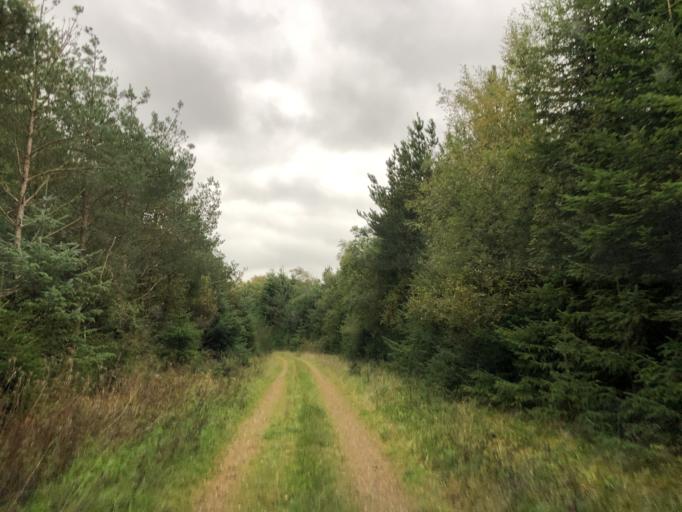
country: DK
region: Central Jutland
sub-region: Holstebro Kommune
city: Ulfborg
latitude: 56.2231
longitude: 8.4439
